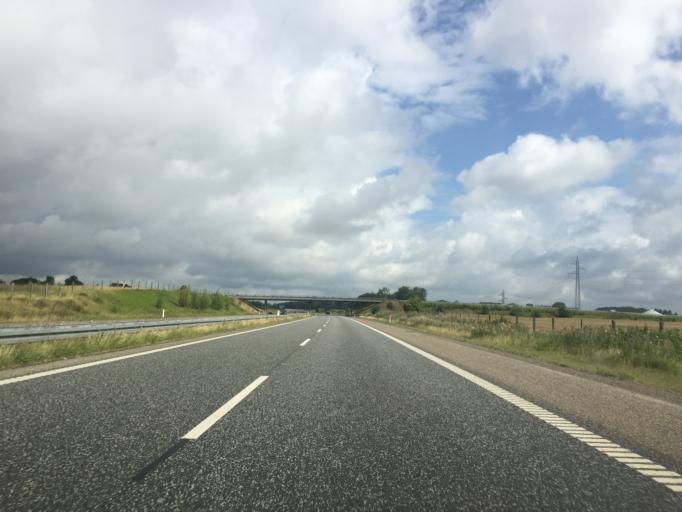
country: DK
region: South Denmark
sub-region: Svendborg Kommune
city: Svendborg
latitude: 55.1260
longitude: 10.5613
